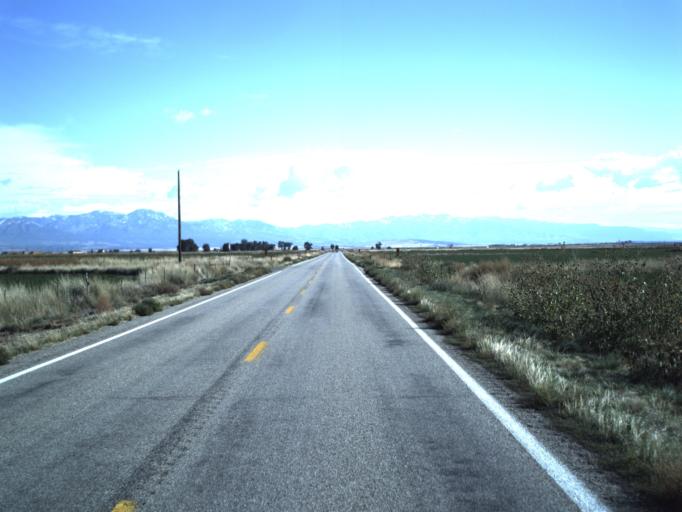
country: US
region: Utah
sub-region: Millard County
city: Delta
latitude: 39.2146
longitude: -112.4168
